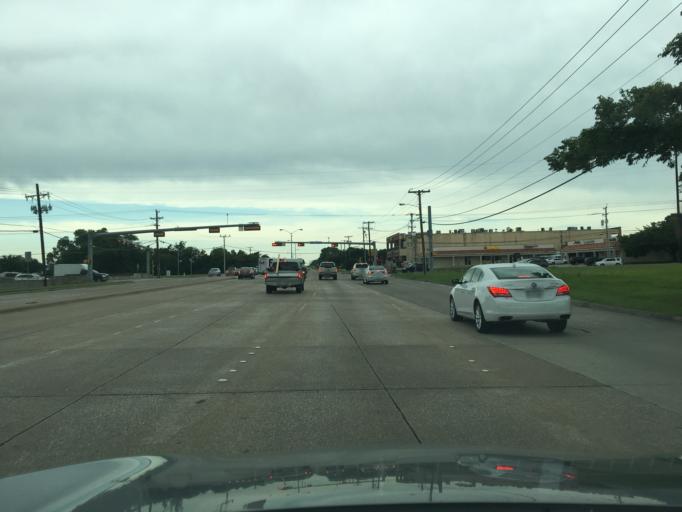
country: US
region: Texas
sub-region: Dallas County
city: Richardson
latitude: 32.9598
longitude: -96.6998
